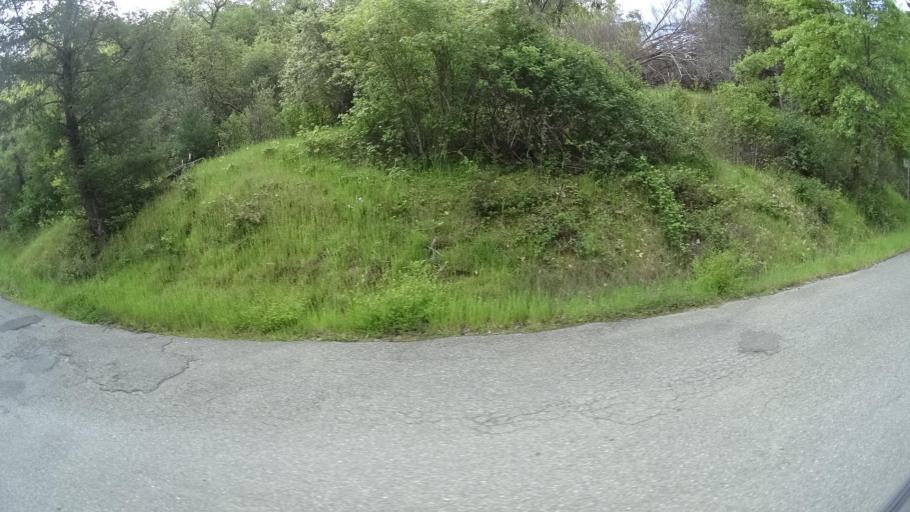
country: US
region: California
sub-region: Humboldt County
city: Redway
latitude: 40.1850
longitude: -123.5889
